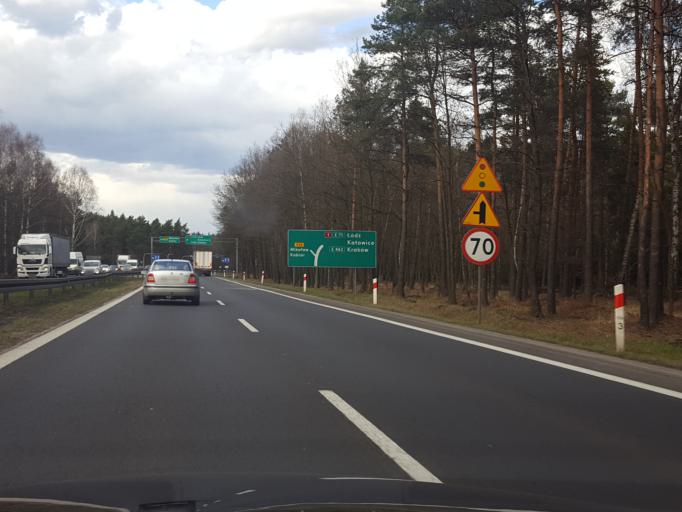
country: PL
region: Silesian Voivodeship
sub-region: Powiat pszczynski
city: Kobior
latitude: 50.0453
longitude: 18.9428
